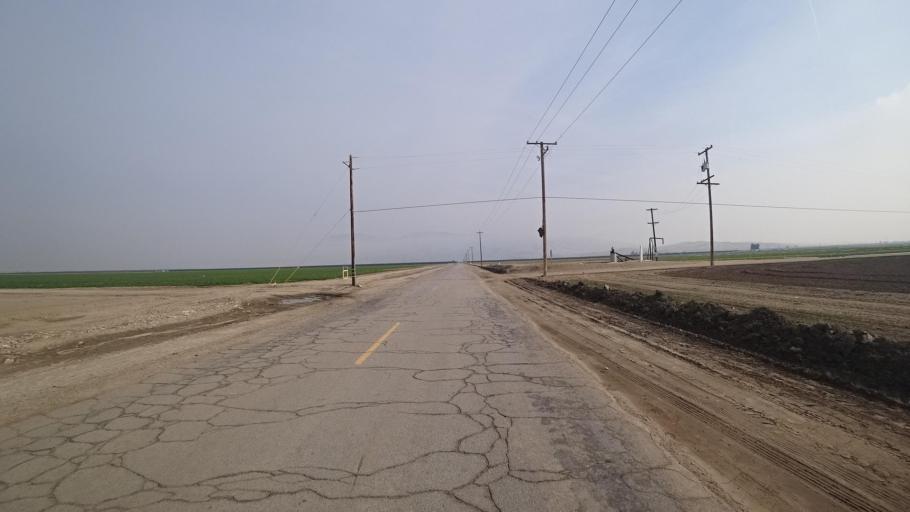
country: US
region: California
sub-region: Kern County
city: Arvin
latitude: 35.1507
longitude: -118.8694
